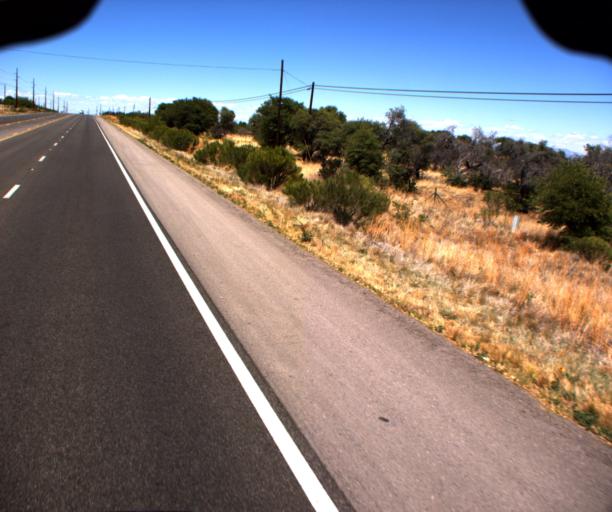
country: US
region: Arizona
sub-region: Cochise County
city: Sierra Vista Southeast
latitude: 31.4183
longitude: -110.2407
